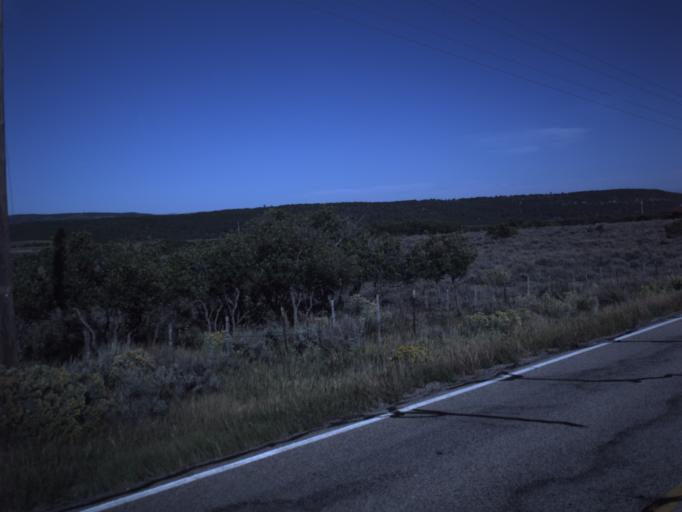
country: US
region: Utah
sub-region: Grand County
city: Moab
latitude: 38.3400
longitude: -109.1691
